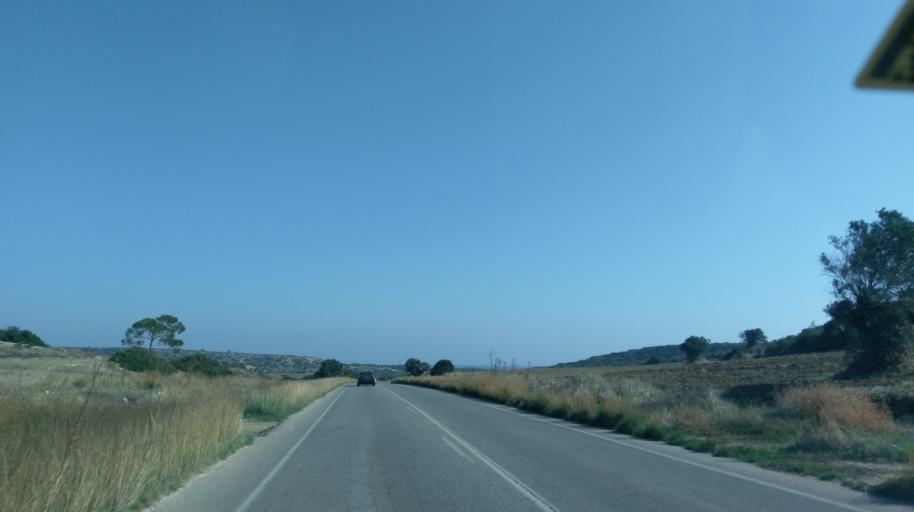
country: CY
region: Ammochostos
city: Leonarisso
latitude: 35.4019
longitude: 34.0856
